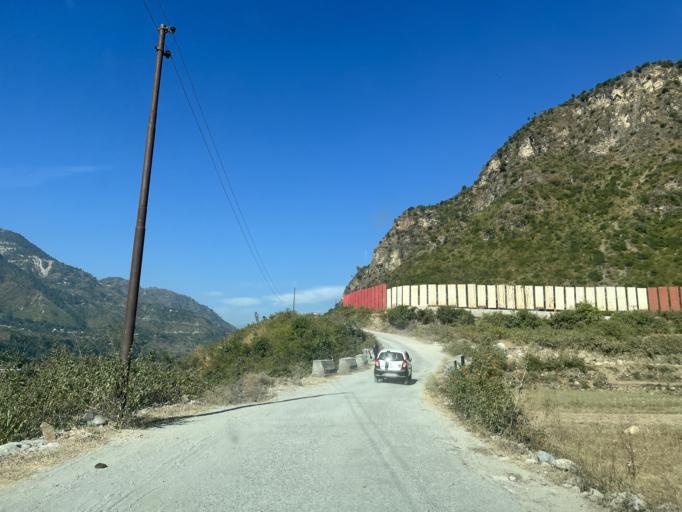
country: IN
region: Uttarakhand
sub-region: Naini Tal
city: Naini Tal
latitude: 29.5088
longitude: 79.4439
